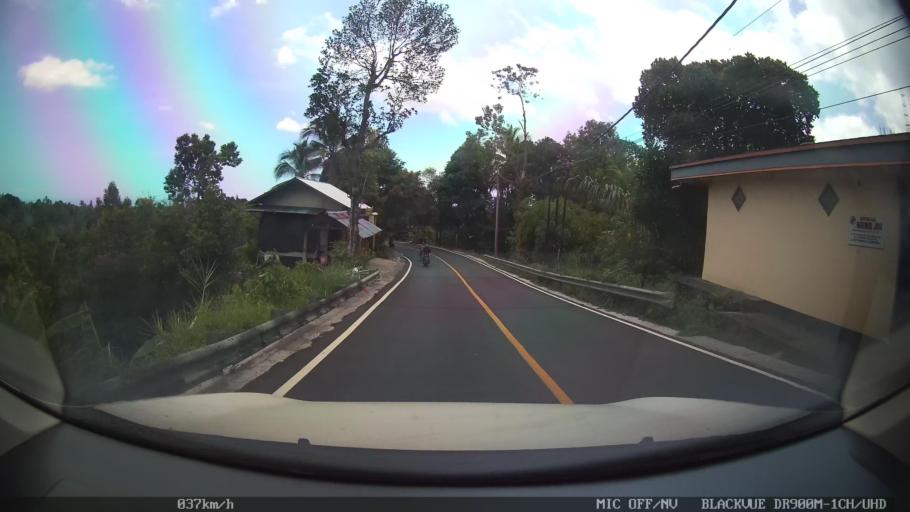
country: ID
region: Bali
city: Banjar Ambengan
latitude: -8.1743
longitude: 115.1269
